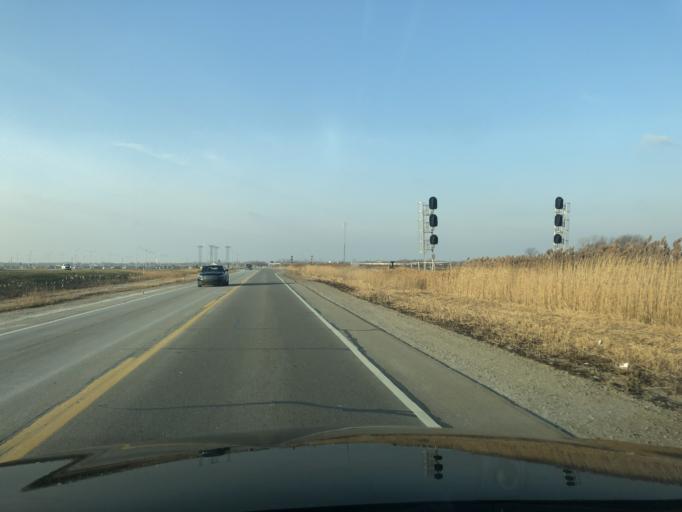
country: US
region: Michigan
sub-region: Wayne County
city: Romulus
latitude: 42.2337
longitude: -83.3528
